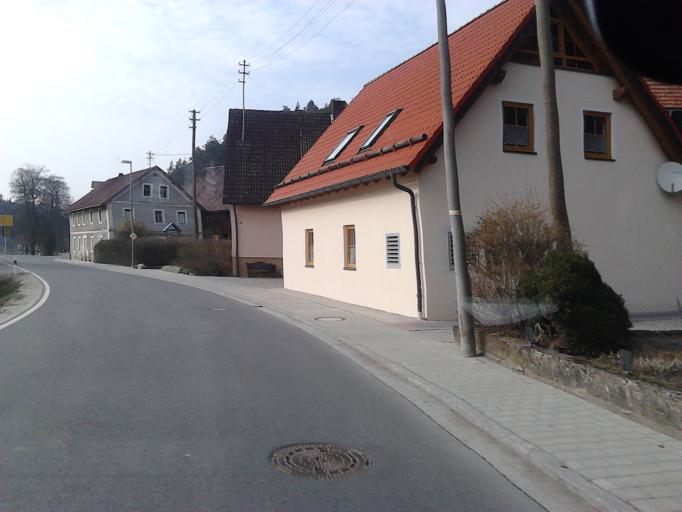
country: DE
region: Bavaria
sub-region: Upper Franconia
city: Stadelhofen
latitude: 49.9662
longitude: 11.1999
